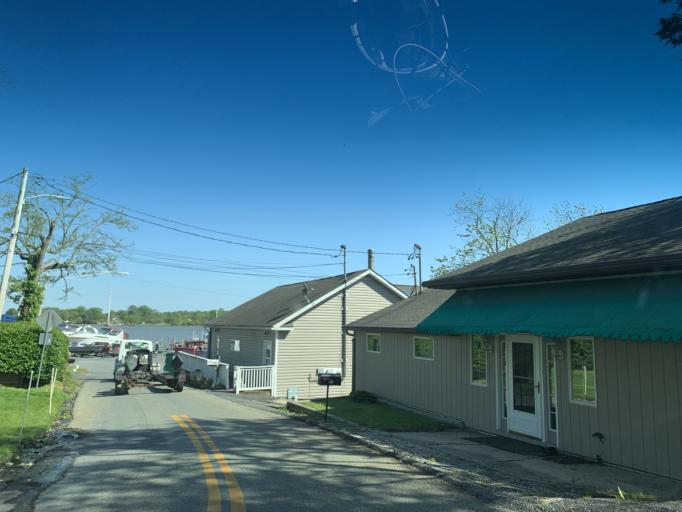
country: US
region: Maryland
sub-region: Harford County
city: Riverside
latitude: 39.4467
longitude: -76.2670
